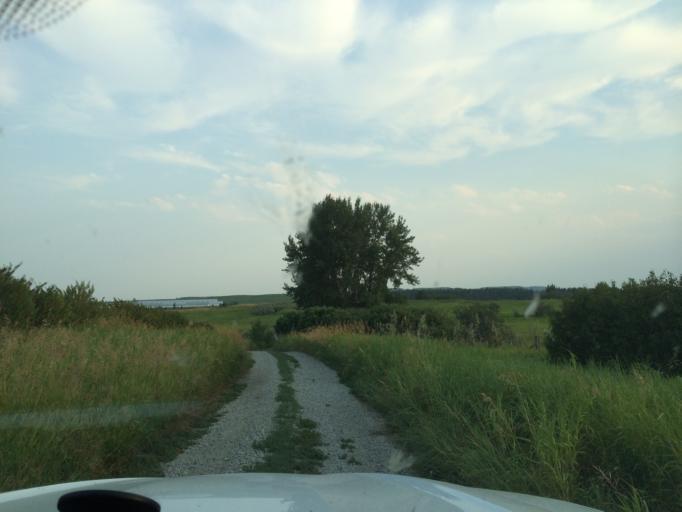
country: CA
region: Alberta
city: Okotoks
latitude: 50.7262
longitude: -114.0248
